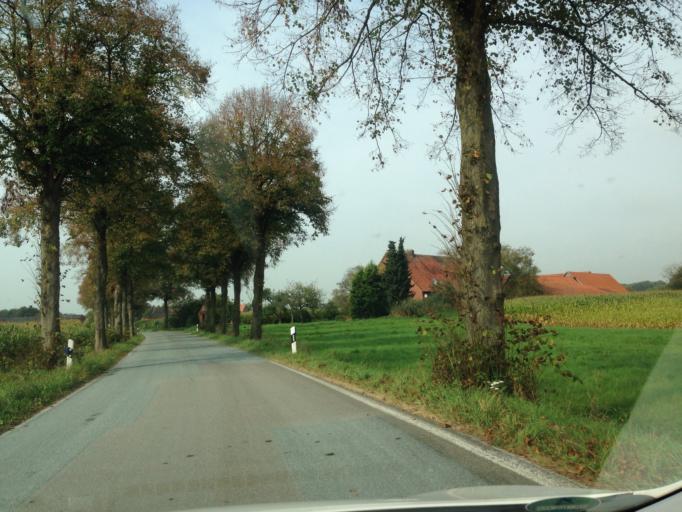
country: DE
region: North Rhine-Westphalia
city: Ludinghausen
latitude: 51.8097
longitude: 7.3992
